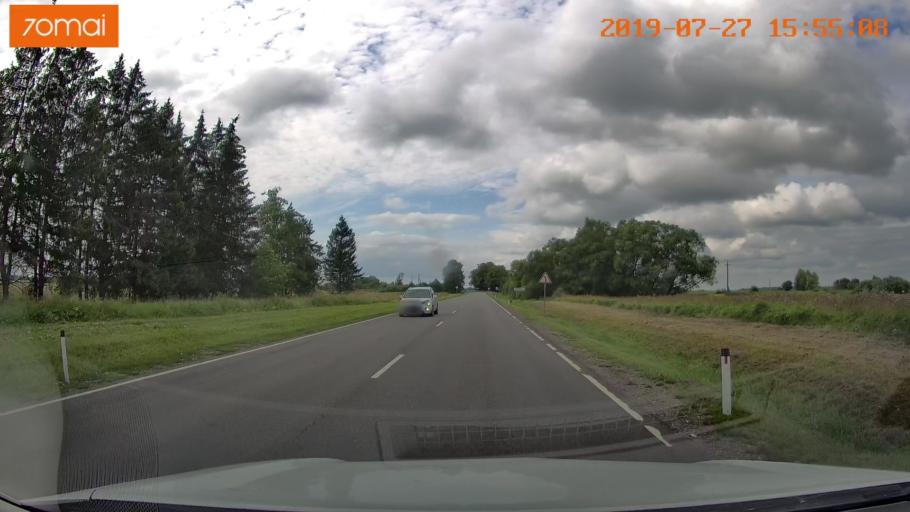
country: RU
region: Kaliningrad
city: Chernyakhovsk
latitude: 54.6121
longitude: 21.9259
